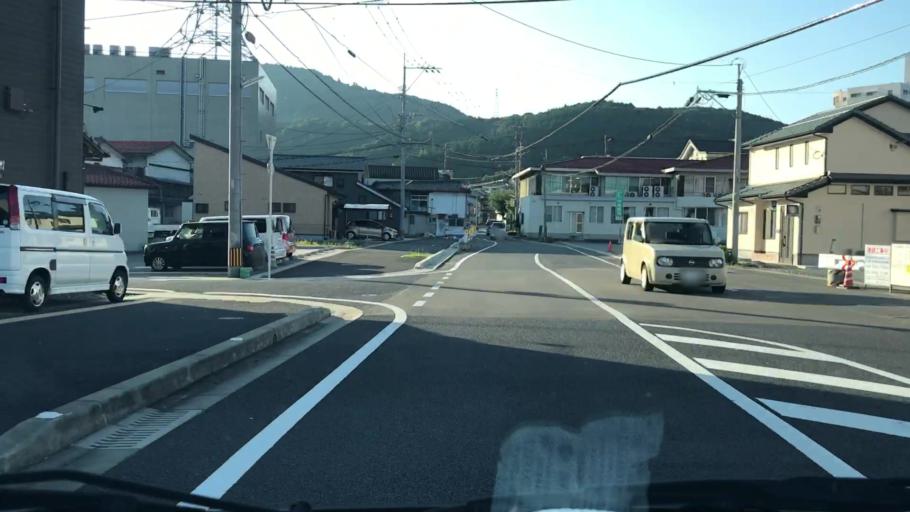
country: JP
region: Saga Prefecture
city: Takeocho-takeo
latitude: 33.1952
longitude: 130.0203
